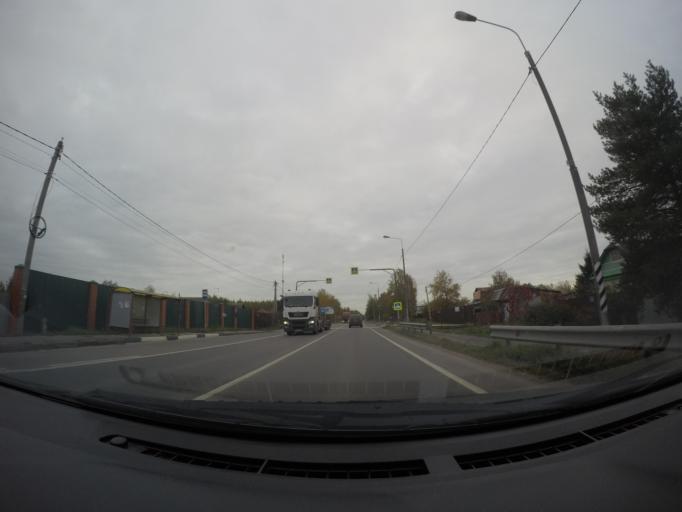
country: RU
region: Moskovskaya
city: Elektrougli
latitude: 55.7260
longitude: 38.2574
